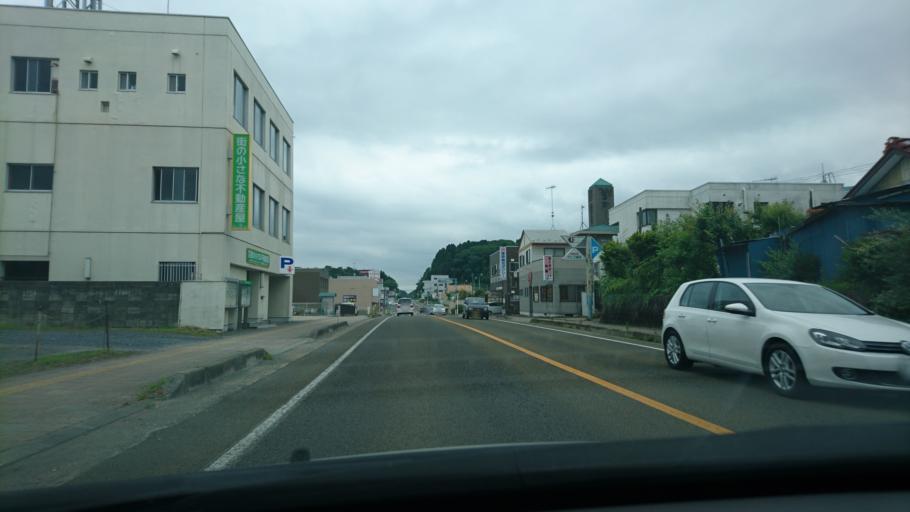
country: JP
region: Miyagi
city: Furukawa
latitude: 38.7310
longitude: 141.0225
